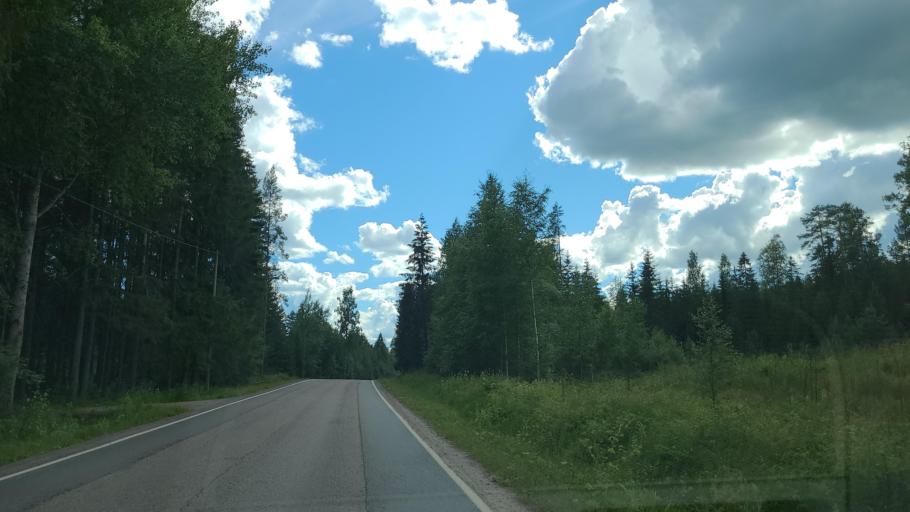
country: FI
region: Central Finland
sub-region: Jaemsae
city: Jaemsae
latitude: 61.9058
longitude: 25.2836
